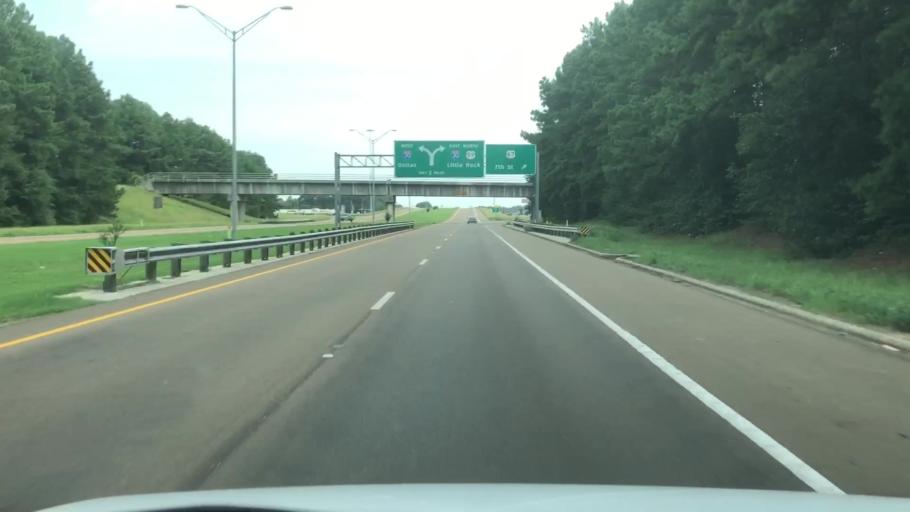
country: US
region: Texas
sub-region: Bowie County
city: Wake Village
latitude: 33.4135
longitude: -94.0969
